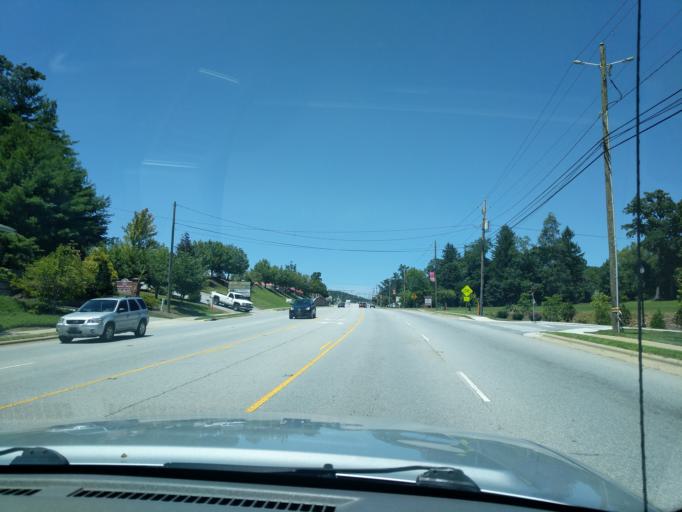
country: US
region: North Carolina
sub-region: Henderson County
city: Fletcher
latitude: 35.4384
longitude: -82.5033
